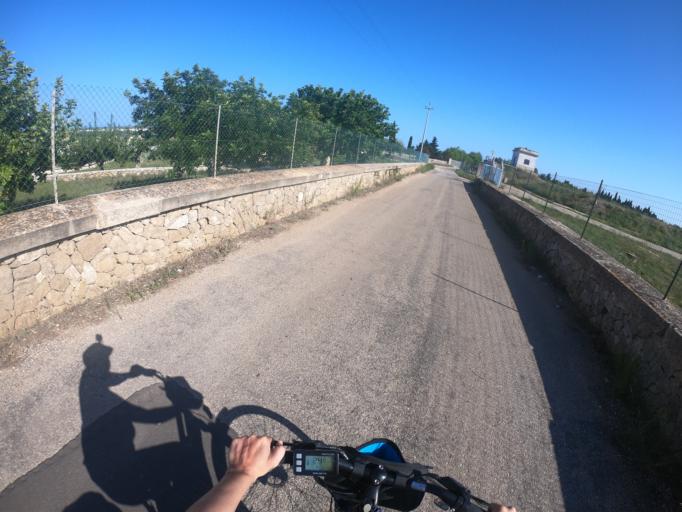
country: IT
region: Apulia
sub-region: Provincia di Lecce
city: Alessano
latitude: 39.8850
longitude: 18.3282
